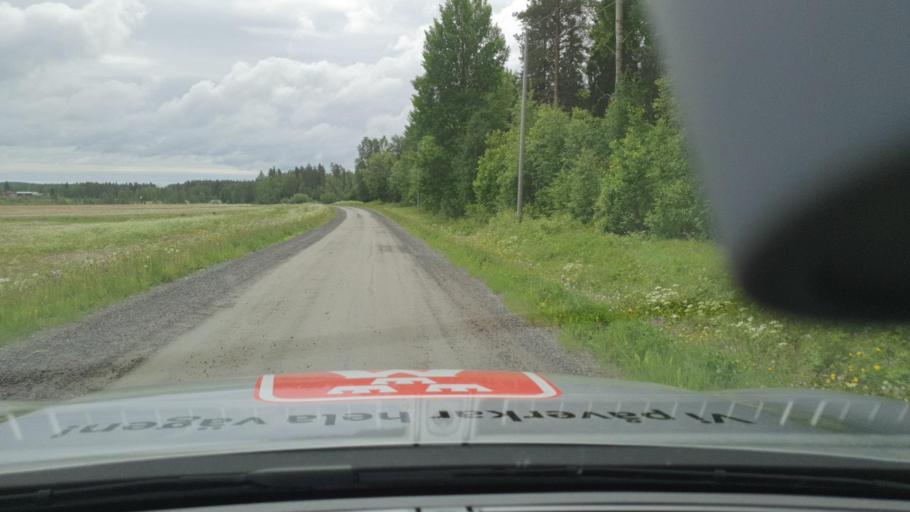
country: SE
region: Norrbotten
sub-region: Lulea Kommun
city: Ranea
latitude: 65.9422
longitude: 22.1128
